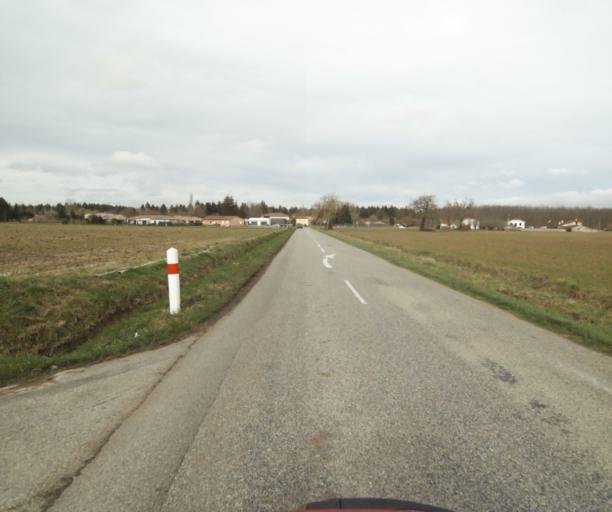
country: FR
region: Midi-Pyrenees
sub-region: Departement de l'Ariege
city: La Tour-du-Crieu
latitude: 43.0829
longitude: 1.7409
